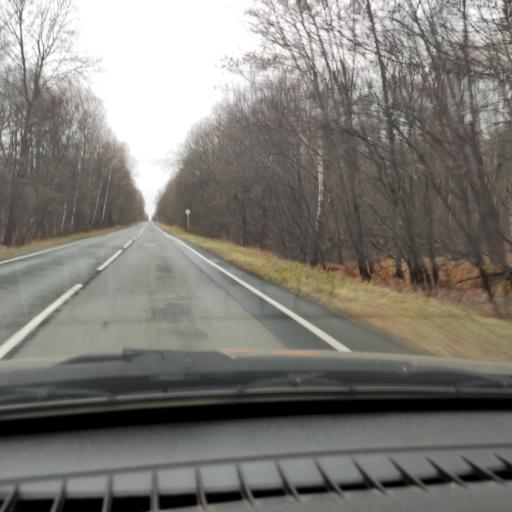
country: RU
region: Samara
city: Zhigulevsk
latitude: 53.3470
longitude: 49.5682
